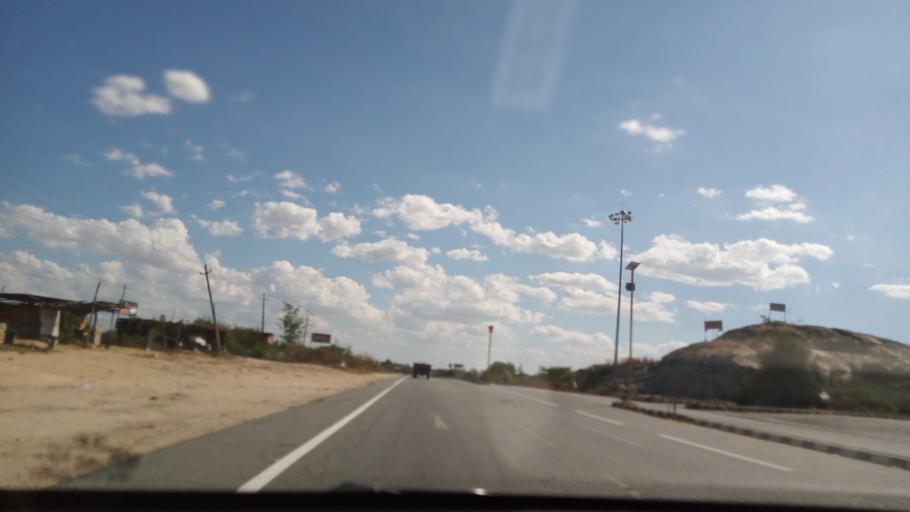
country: IN
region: Karnataka
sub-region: Kolar
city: Mulbagal
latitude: 13.1725
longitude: 78.4086
